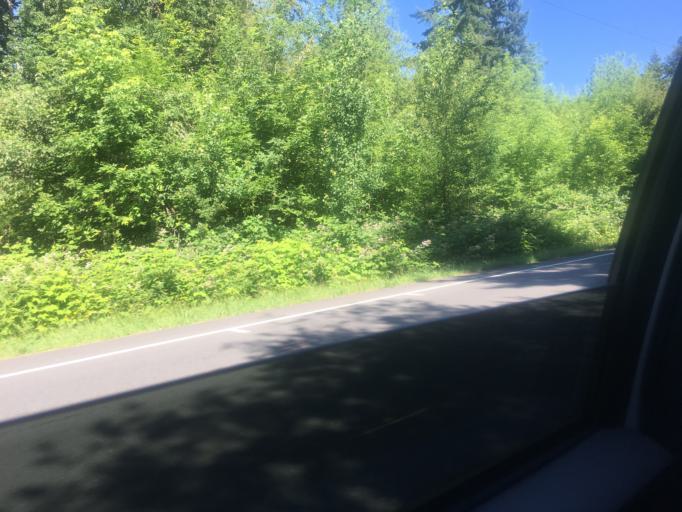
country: US
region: Washington
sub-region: King County
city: Bellevue
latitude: 47.6103
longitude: -122.1749
